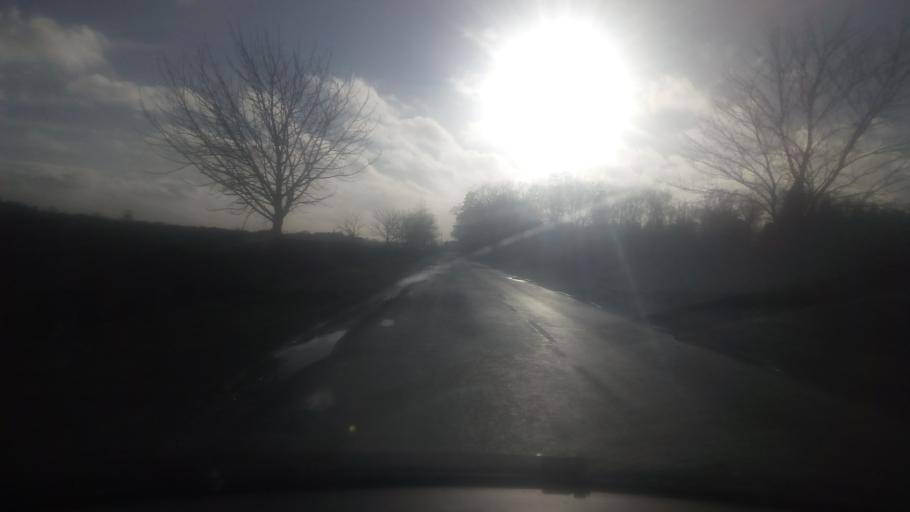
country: GB
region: Scotland
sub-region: The Scottish Borders
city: Coldstream
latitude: 55.6969
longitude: -2.3203
